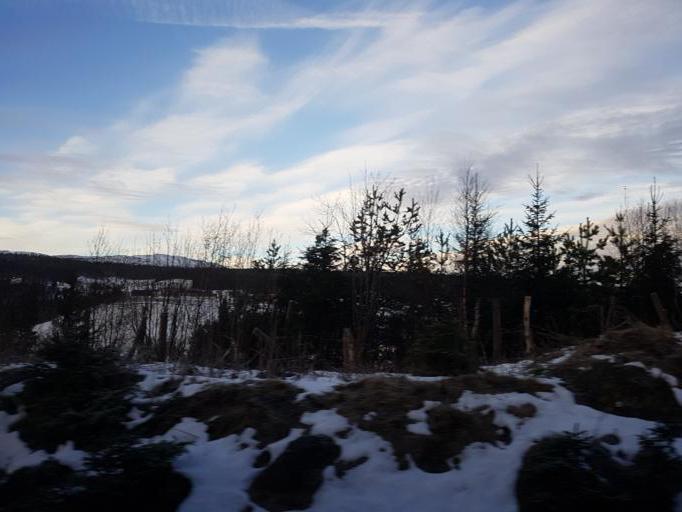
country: NO
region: Sor-Trondelag
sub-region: Rennebu
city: Berkak
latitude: 62.7516
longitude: 9.9851
